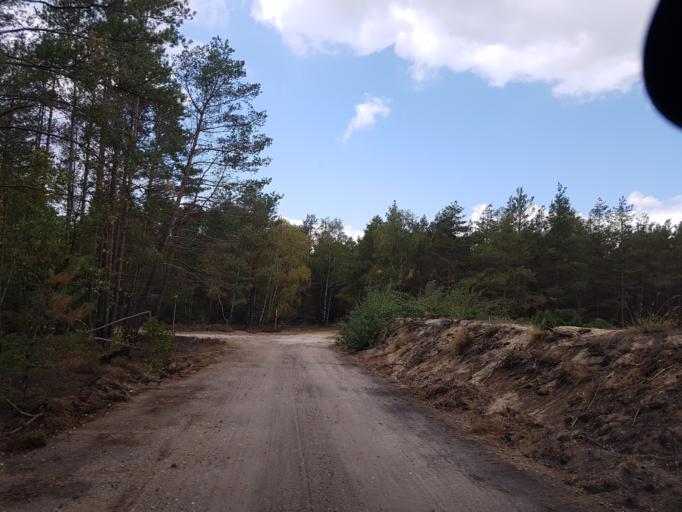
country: DE
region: Brandenburg
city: Finsterwalde
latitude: 51.5878
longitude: 13.7578
